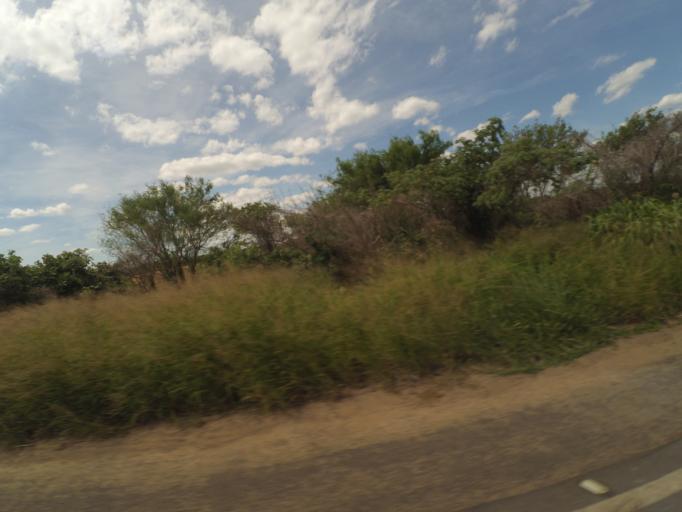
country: BO
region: Santa Cruz
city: Pailon
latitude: -17.5856
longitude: -62.0506
